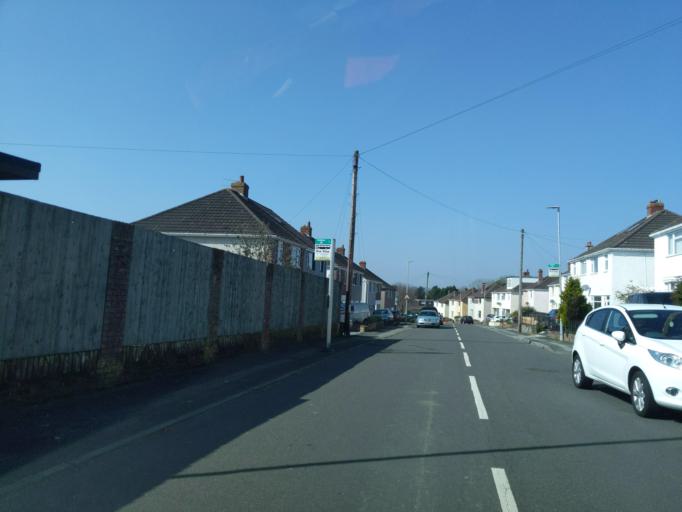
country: GB
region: England
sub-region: Devon
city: Plympton
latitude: 50.3954
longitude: -4.0754
